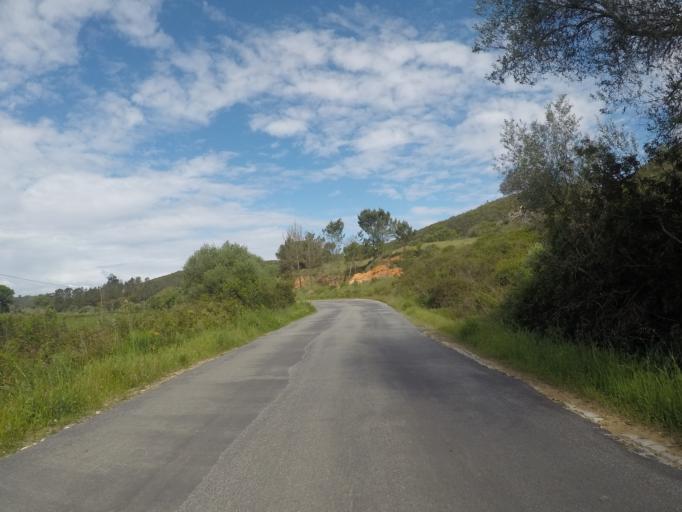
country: PT
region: Beja
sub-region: Odemira
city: Sao Teotonio
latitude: 37.4369
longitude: -8.7708
